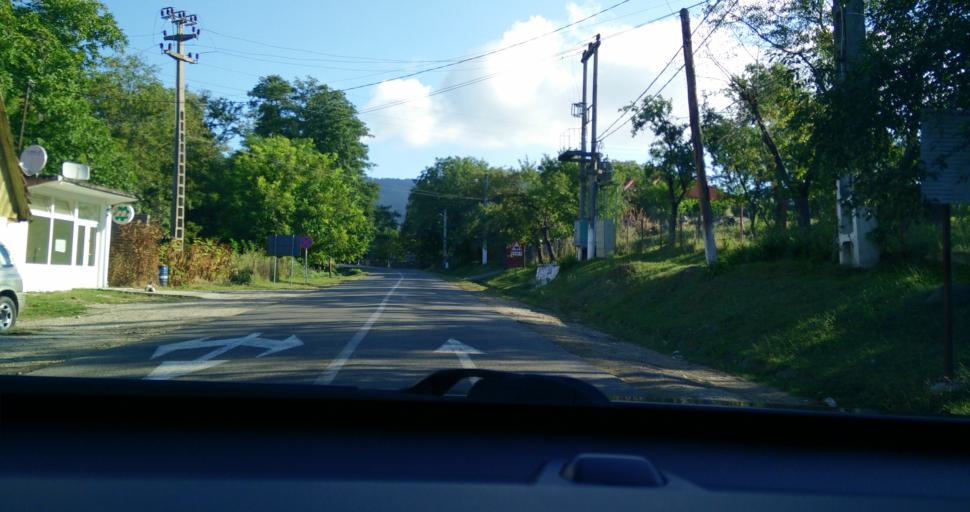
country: RO
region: Gorj
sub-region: Comuna Baia de Fier
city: Baia de Fier
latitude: 45.1716
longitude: 23.7545
